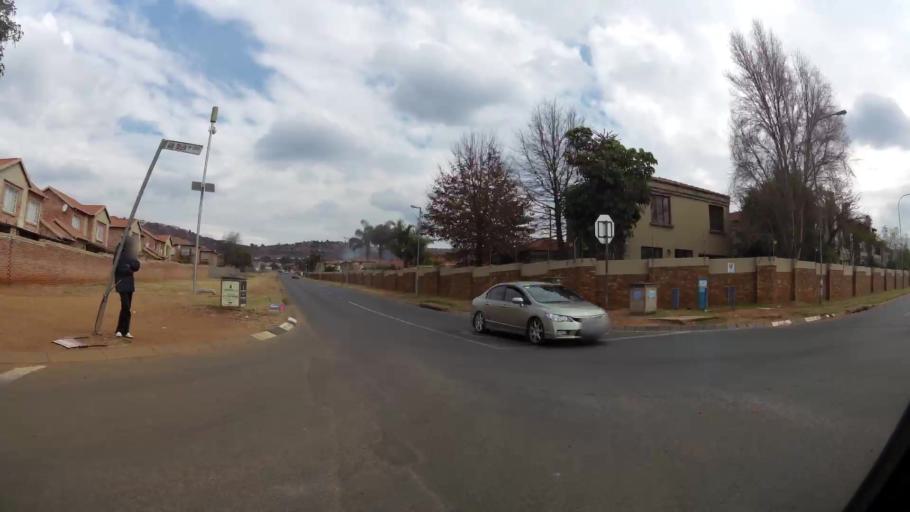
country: ZA
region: Gauteng
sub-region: City of Johannesburg Metropolitan Municipality
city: Roodepoort
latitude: -26.0957
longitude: 27.8776
